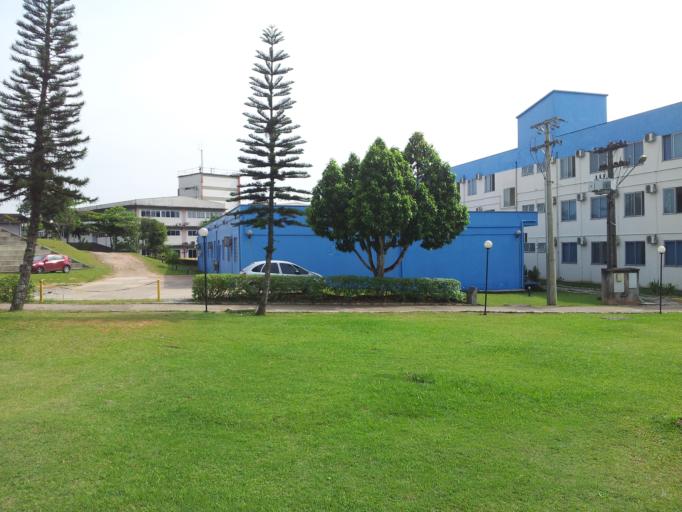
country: BR
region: Santa Catarina
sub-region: Joinville
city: Joinville
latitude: -26.2531
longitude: -48.8554
